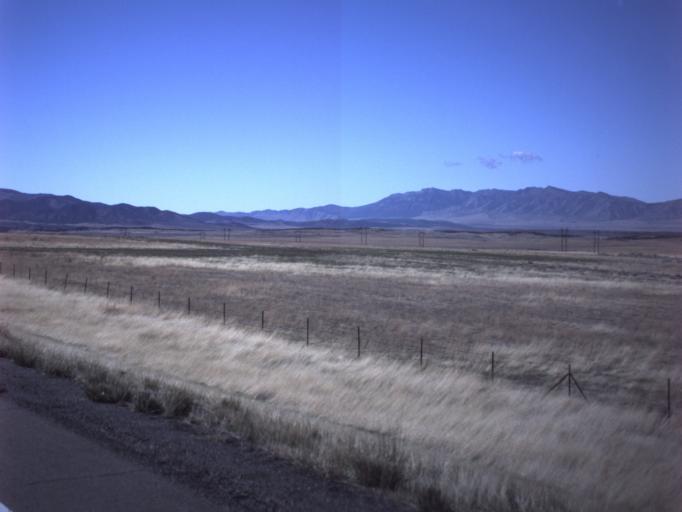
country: US
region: Utah
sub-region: Sanpete County
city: Gunnison
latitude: 39.4266
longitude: -111.9199
